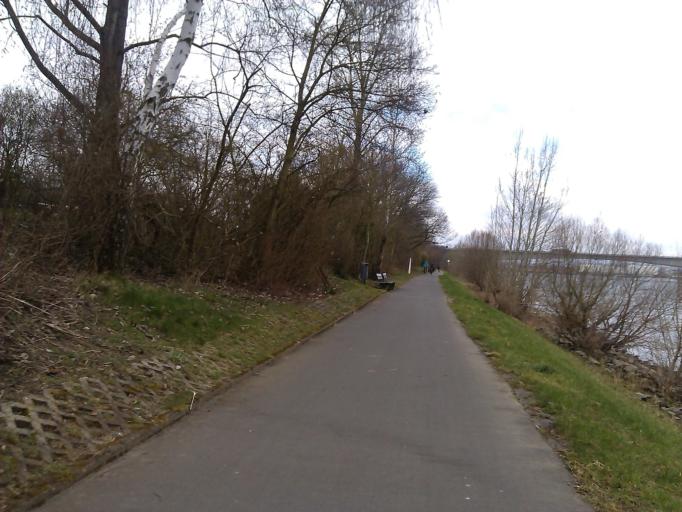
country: DE
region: Rheinland-Pfalz
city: Sankt Sebastian
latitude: 50.4029
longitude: 7.5782
